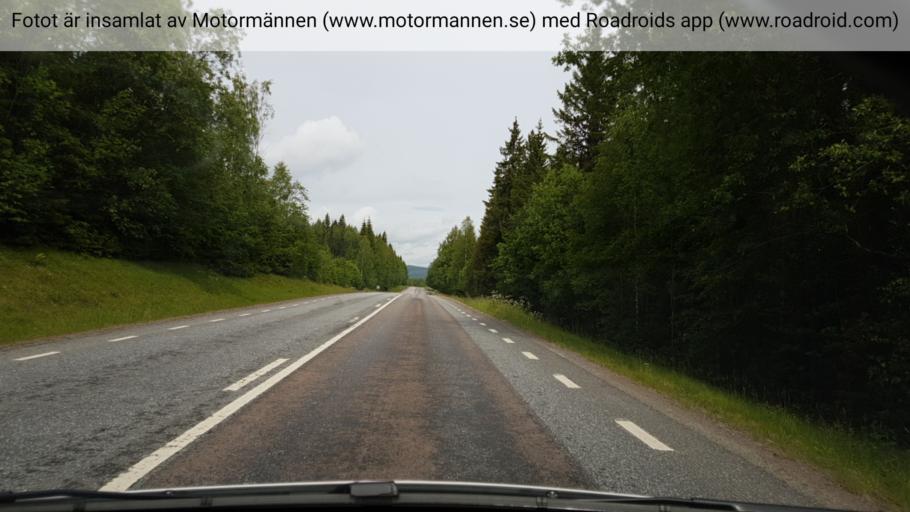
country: SE
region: Vaesternorrland
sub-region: Solleftea Kommun
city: Solleftea
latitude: 63.3010
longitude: 17.2097
